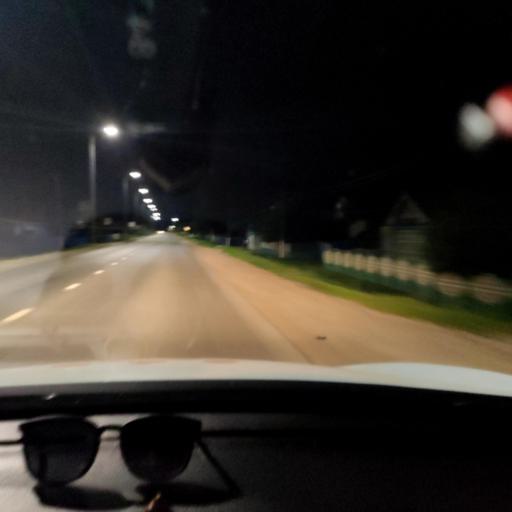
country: RU
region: Tatarstan
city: Rybnaya Sloboda
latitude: 55.4287
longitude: 49.8894
